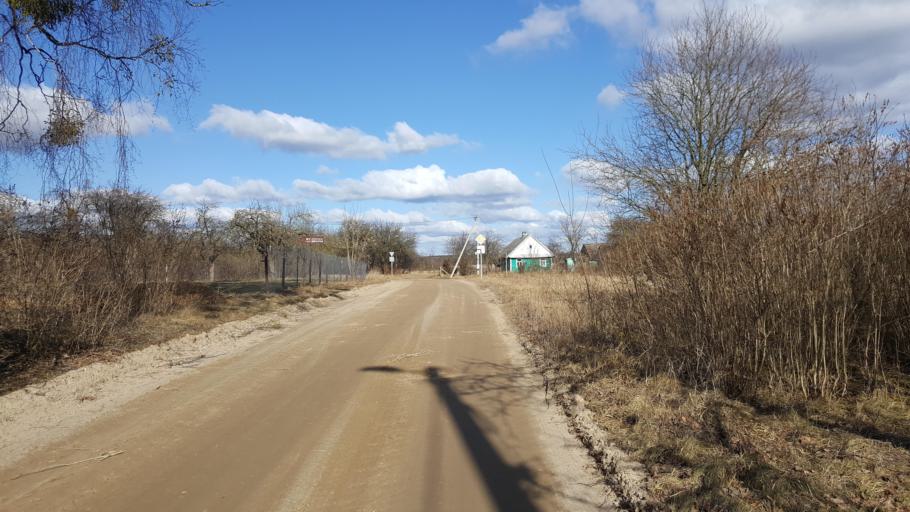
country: BY
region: Brest
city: Kamyanyets
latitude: 52.3883
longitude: 23.8855
